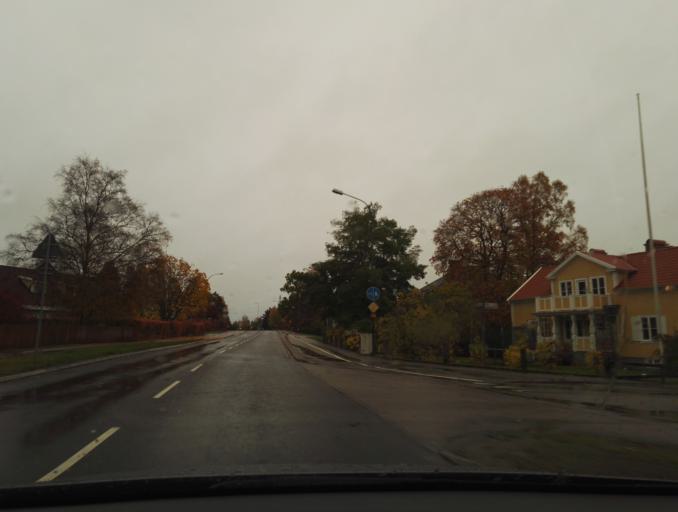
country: SE
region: Kronoberg
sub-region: Vaxjo Kommun
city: Vaexjoe
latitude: 56.8848
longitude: 14.7528
